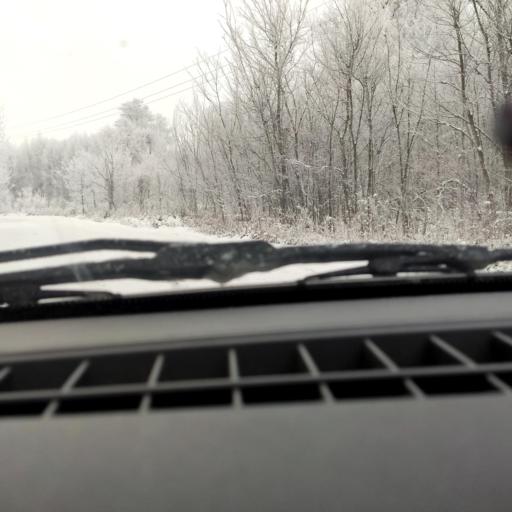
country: RU
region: Bashkortostan
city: Ufa
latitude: 54.7166
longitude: 56.1327
